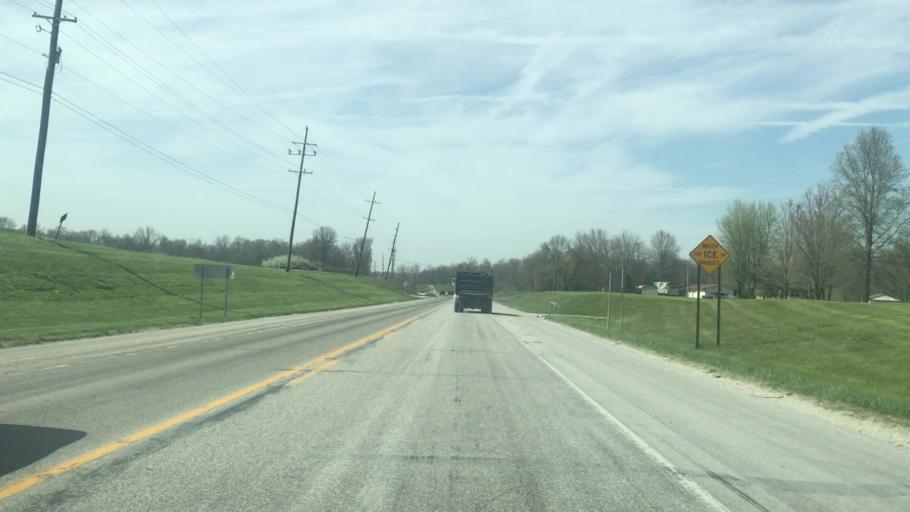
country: US
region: Indiana
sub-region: Putnam County
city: Cloverdale
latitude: 39.5449
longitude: -86.8065
